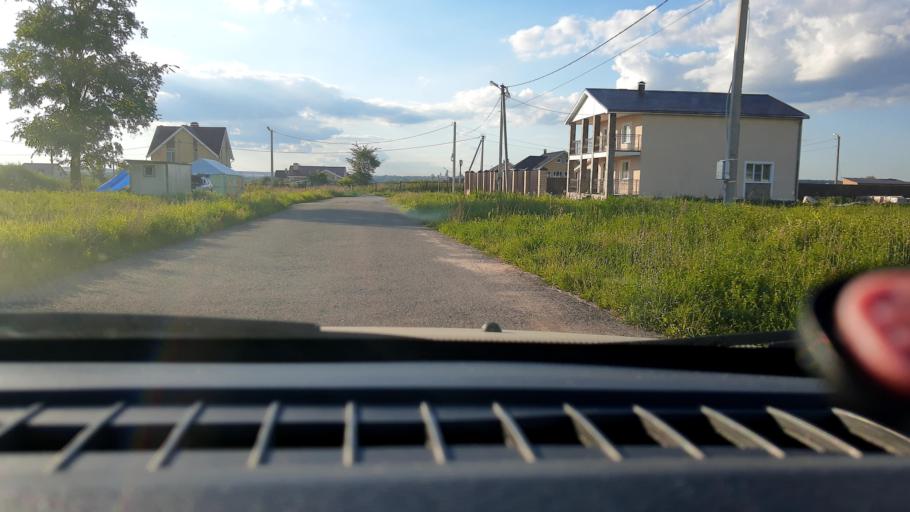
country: RU
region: Nizjnij Novgorod
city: Burevestnik
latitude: 56.0393
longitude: 43.8850
